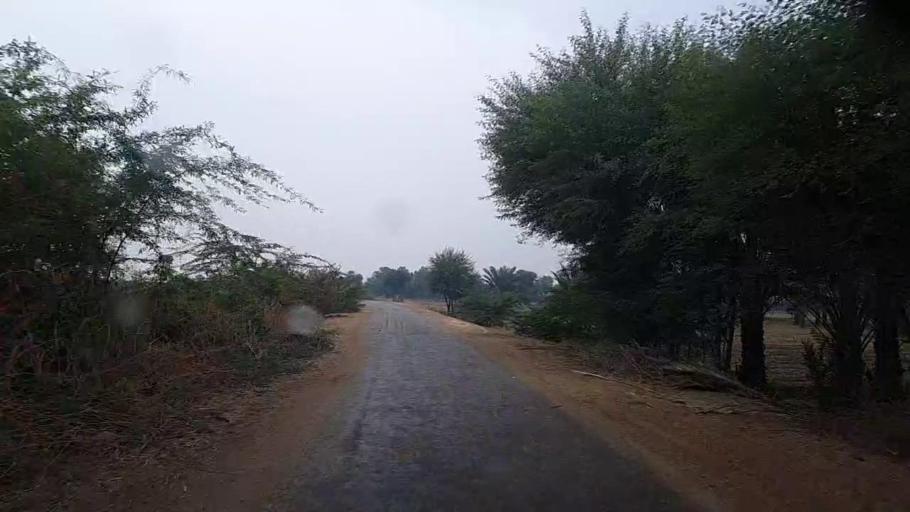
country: PK
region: Sindh
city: Ranipur
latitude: 27.2600
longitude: 68.5753
